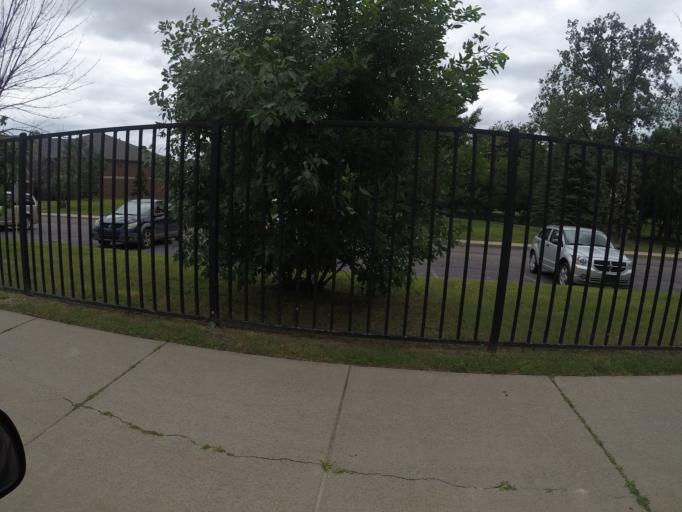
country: US
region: Michigan
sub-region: Wayne County
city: River Rouge
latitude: 42.3071
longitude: -83.1380
